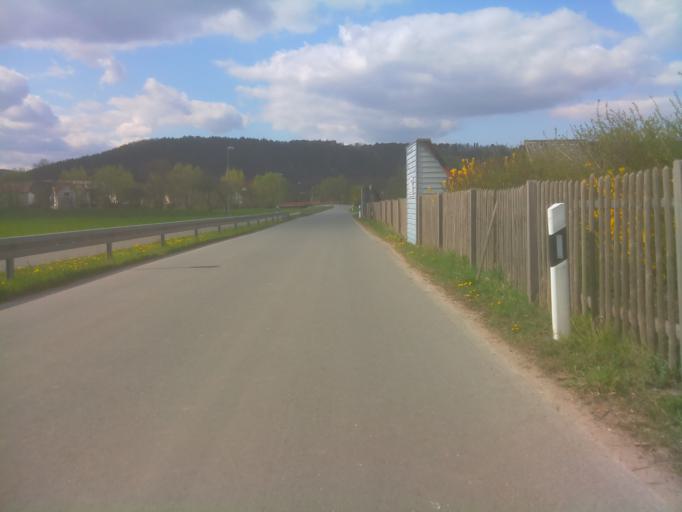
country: DE
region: Thuringia
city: Schops
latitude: 50.8328
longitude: 11.6018
